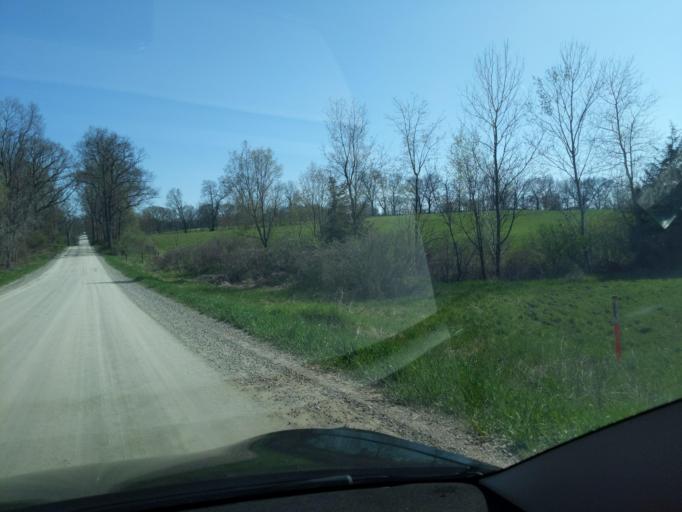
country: US
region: Michigan
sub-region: Washtenaw County
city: Chelsea
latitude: 42.3980
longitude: -84.0837
